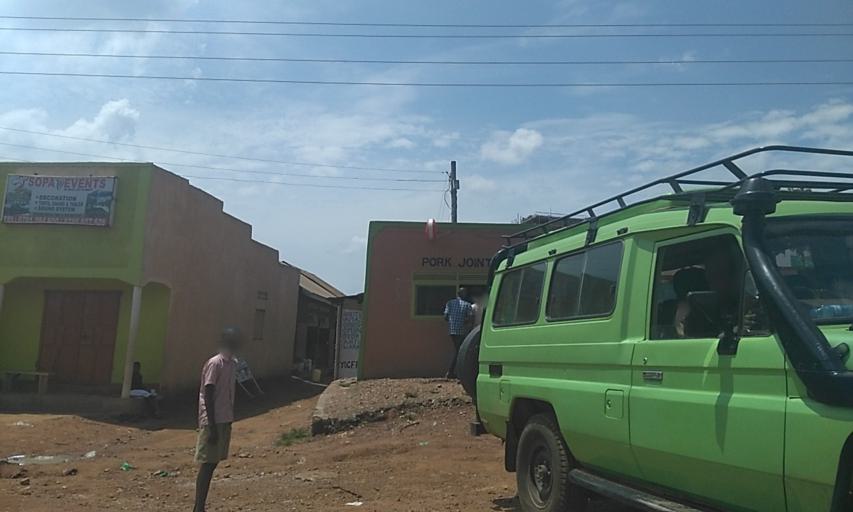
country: UG
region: Central Region
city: Kampala Central Division
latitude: 0.3557
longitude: 32.5346
